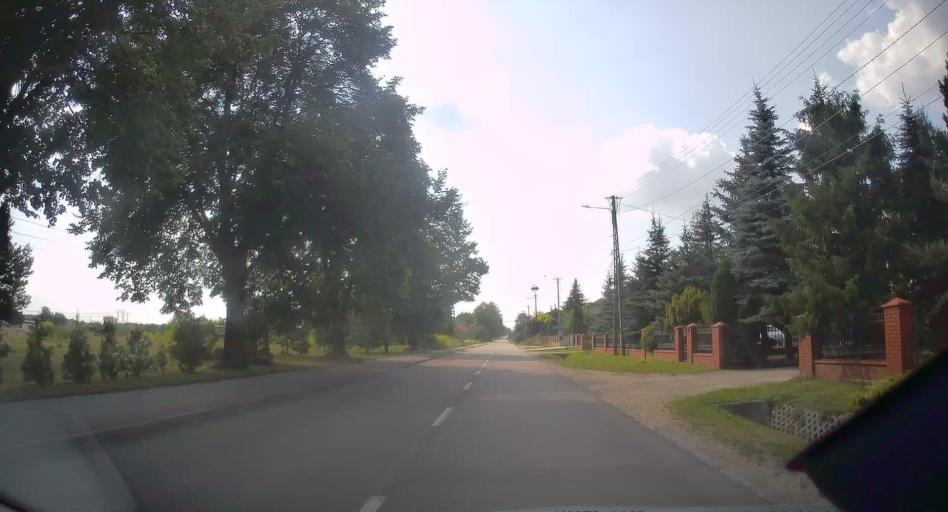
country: PL
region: Swietokrzyskie
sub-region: Powiat jedrzejowski
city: Malogoszcz
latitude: 50.8665
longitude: 20.2976
